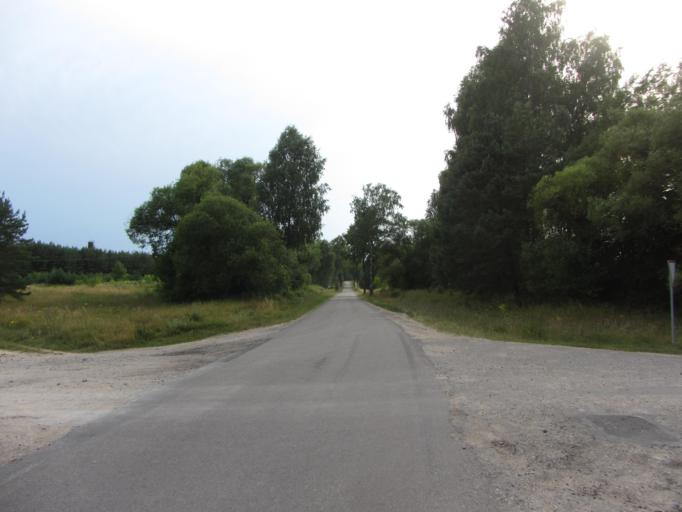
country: LT
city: Veisiejai
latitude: 54.0001
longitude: 23.6649
